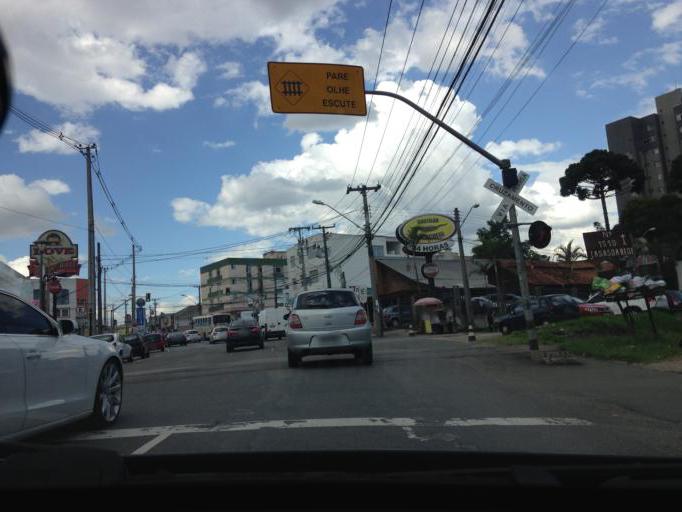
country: BR
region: Parana
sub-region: Curitiba
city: Curitiba
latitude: -25.4051
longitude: -49.2461
